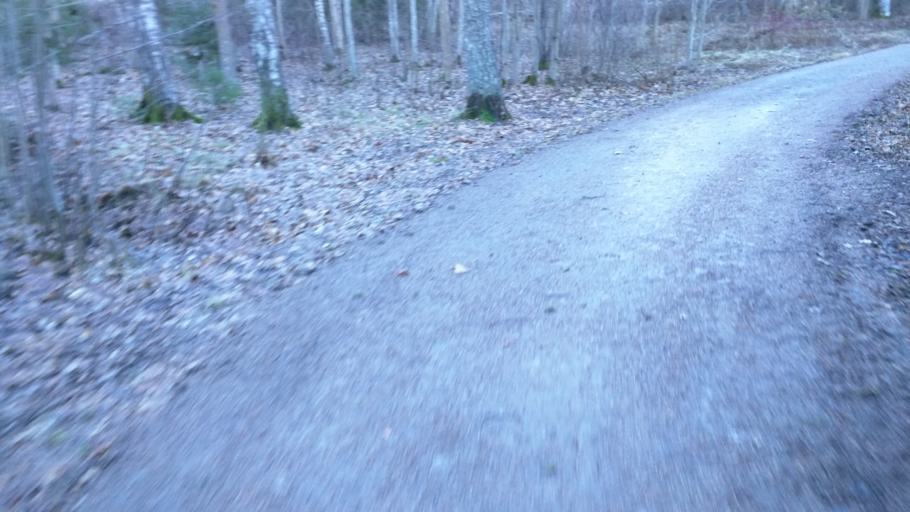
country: FI
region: Uusimaa
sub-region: Helsinki
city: Kauniainen
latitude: 60.2367
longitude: 24.7154
